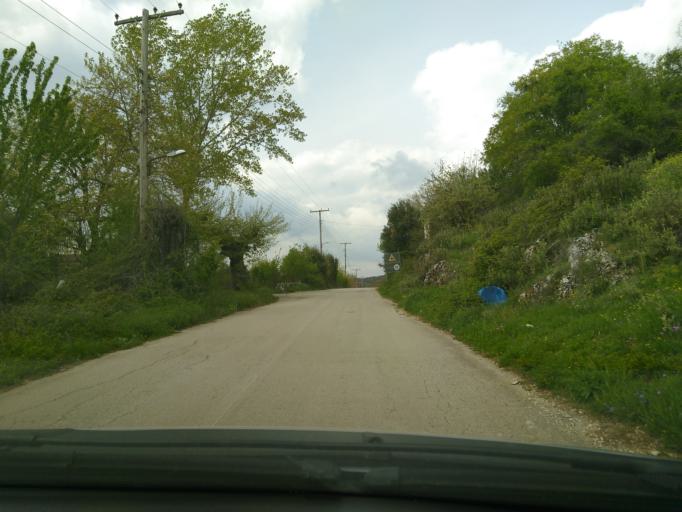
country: GR
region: Epirus
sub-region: Nomos Ioanninon
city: Asprangeloi
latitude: 39.7767
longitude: 20.6887
